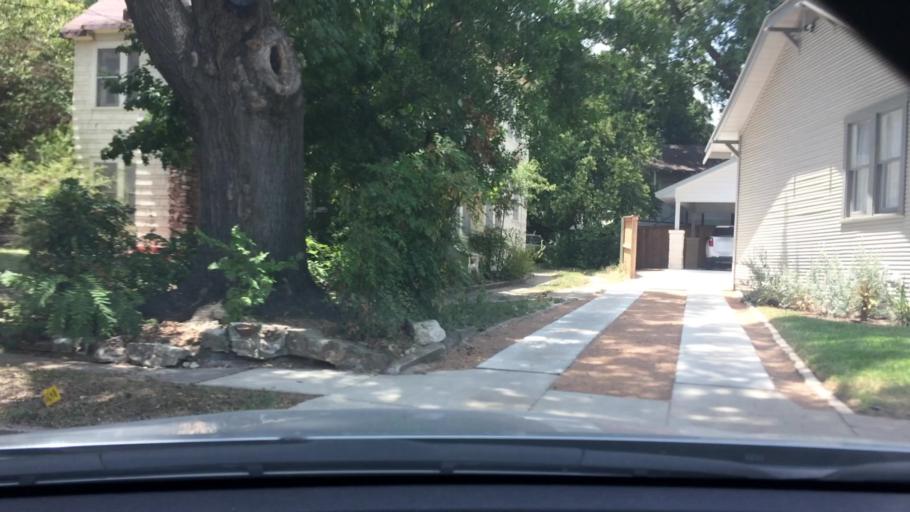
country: US
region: Texas
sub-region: Bexar County
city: Olmos Park
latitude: 29.4562
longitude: -98.4854
